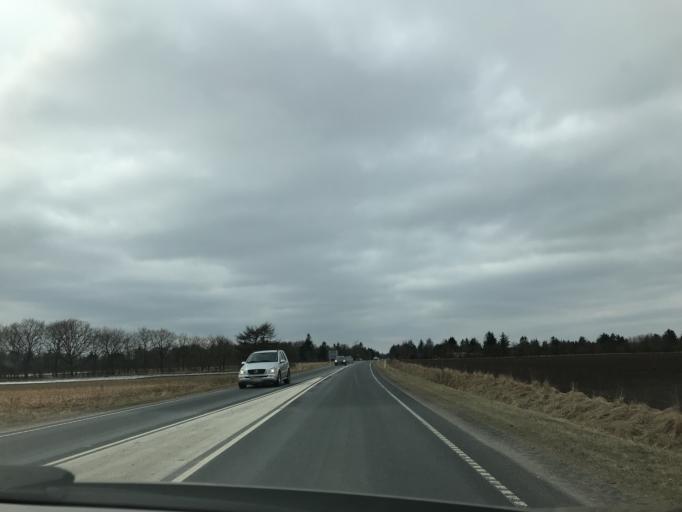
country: DK
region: South Denmark
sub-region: Billund Kommune
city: Grindsted
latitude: 55.8414
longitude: 8.8678
